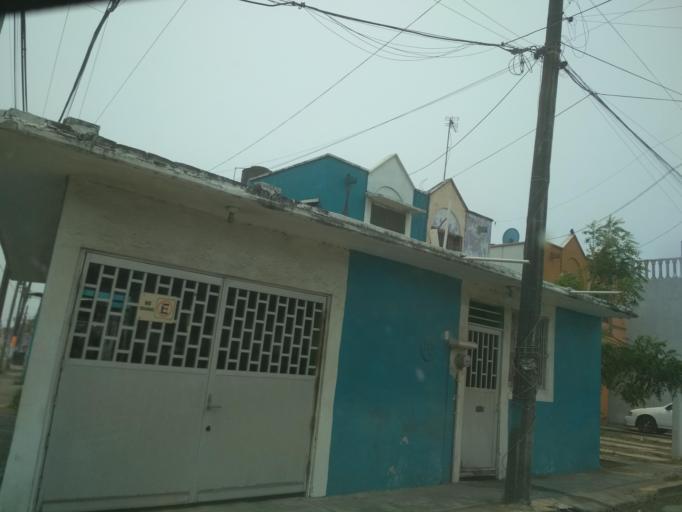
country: MX
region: Veracruz
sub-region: Veracruz
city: Rio Medio [Granja]
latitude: 19.2120
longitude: -96.2039
